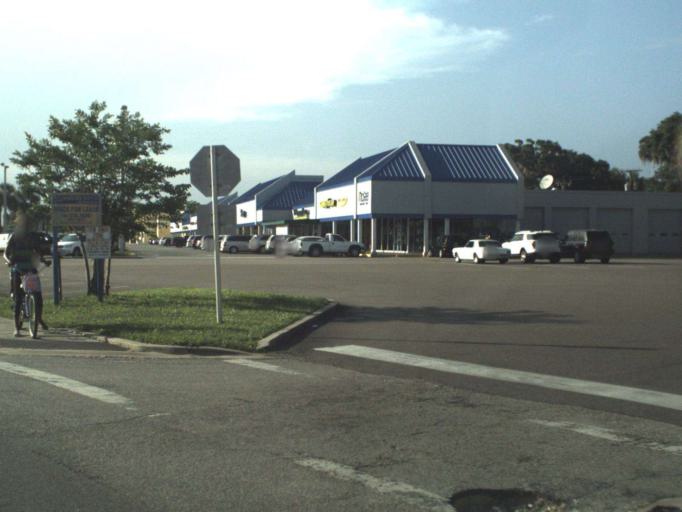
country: US
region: Florida
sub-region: Volusia County
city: New Smyrna Beach
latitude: 29.0070
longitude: -80.9181
